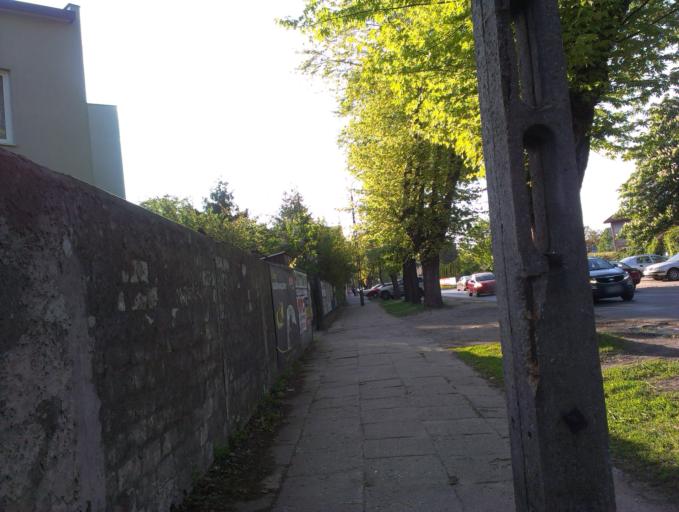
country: PL
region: Masovian Voivodeship
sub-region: Powiat piaseczynski
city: Piaseczno
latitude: 52.0660
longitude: 21.0311
